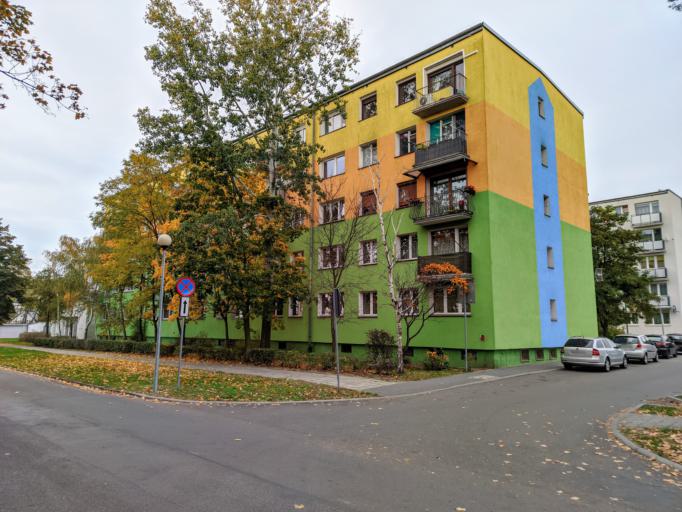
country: PL
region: Lubusz
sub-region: Powiat nowosolski
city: Nowa Sol
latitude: 51.8003
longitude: 15.7004
